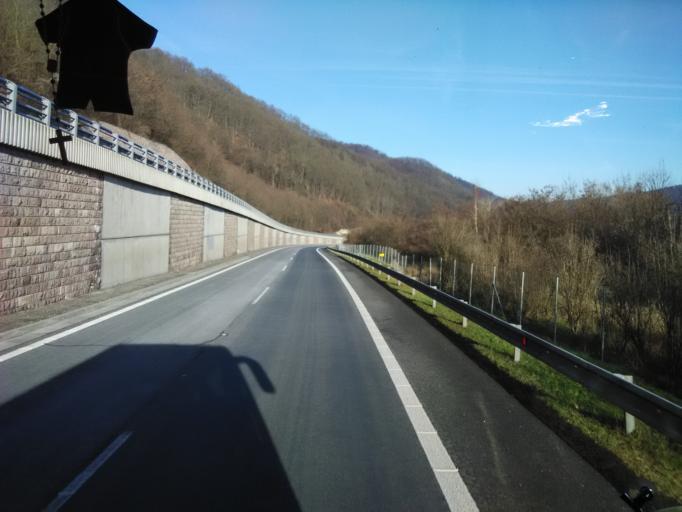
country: SK
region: Banskobystricky
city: Nova Bana
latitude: 48.4316
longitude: 18.6740
